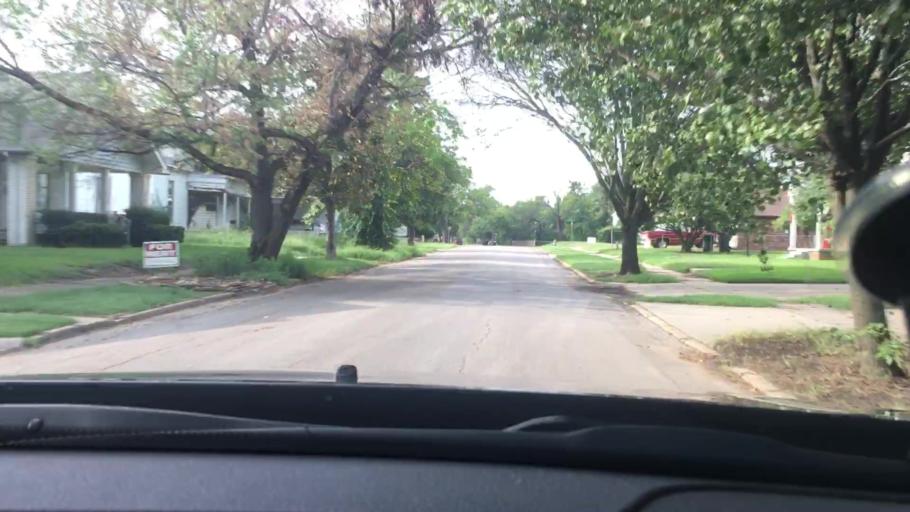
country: US
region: Oklahoma
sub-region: Carter County
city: Ardmore
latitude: 34.1786
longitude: -97.1292
